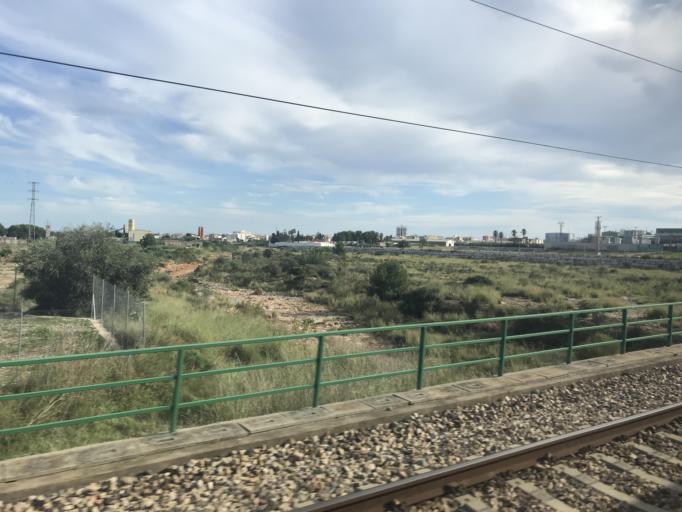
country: ES
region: Valencia
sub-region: Provincia de Castello
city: Benicarlo
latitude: 40.4321
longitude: 0.4191
